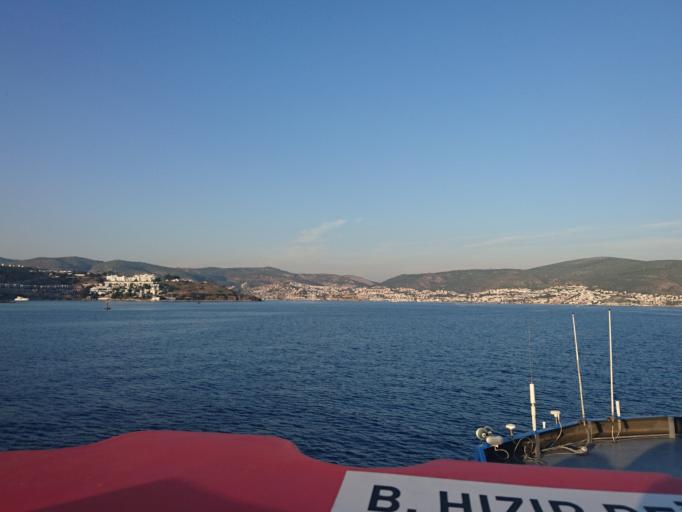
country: TR
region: Mugla
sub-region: Bodrum
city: Bodrum
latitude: 37.0112
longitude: 27.4132
